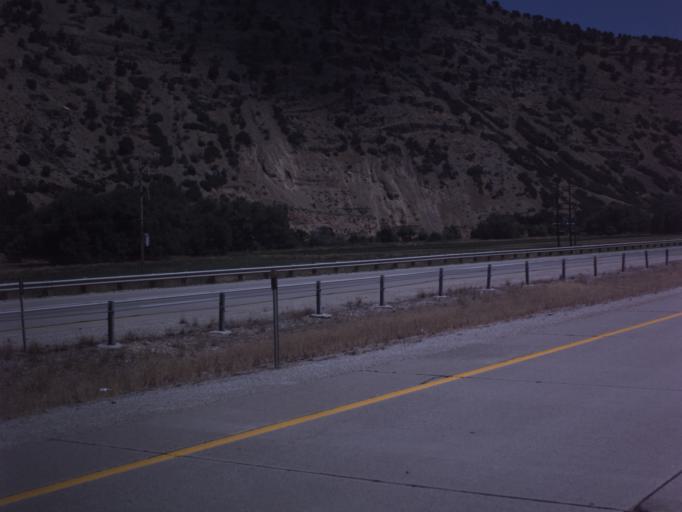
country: US
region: Utah
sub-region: Morgan County
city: Morgan
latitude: 41.0510
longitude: -111.6213
